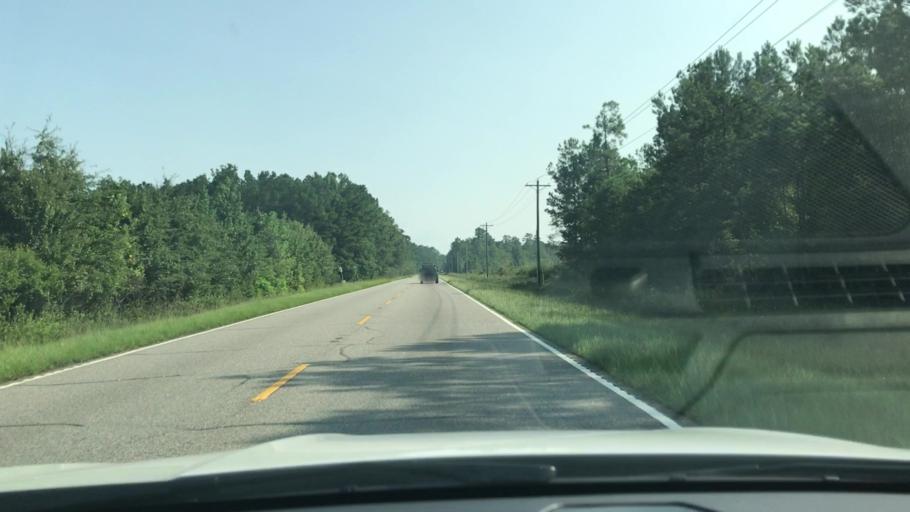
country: US
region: South Carolina
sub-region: Georgetown County
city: Georgetown
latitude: 33.5188
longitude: -79.2470
